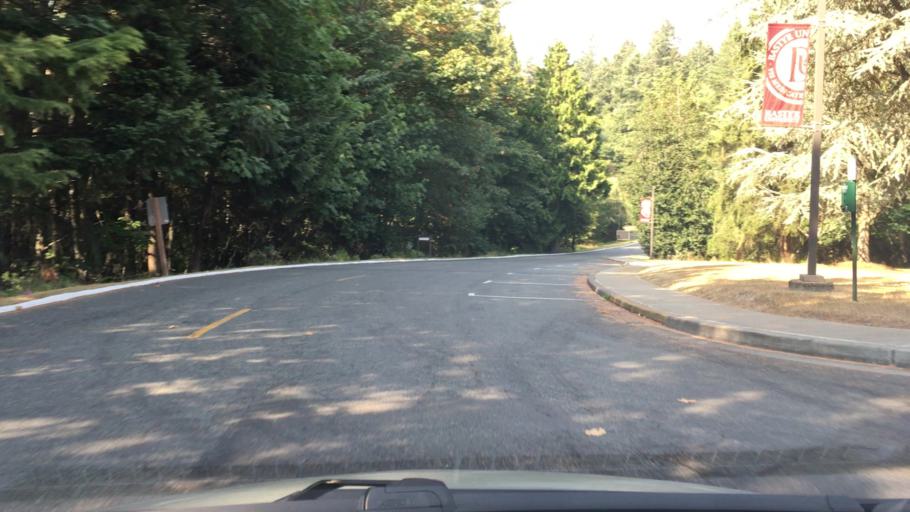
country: US
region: Washington
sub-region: King County
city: Inglewood-Finn Hill
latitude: 47.7312
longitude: -122.2529
